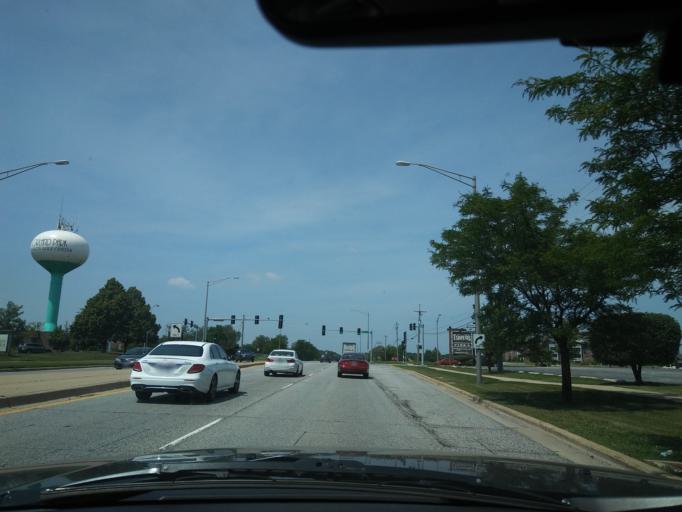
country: US
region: Illinois
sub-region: Cook County
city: Tinley Park
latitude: 41.6082
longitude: -87.7942
